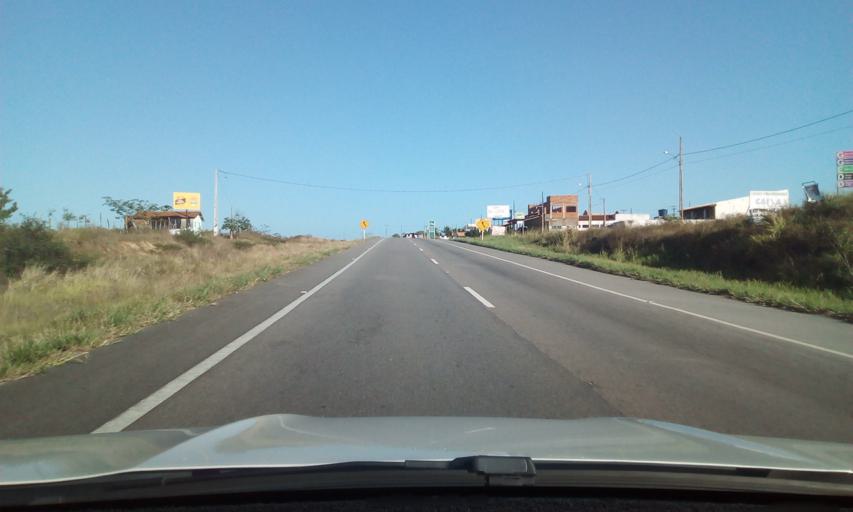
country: BR
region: Paraiba
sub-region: Gurinhem
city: Gurinhem
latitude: -7.1693
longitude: -35.3323
